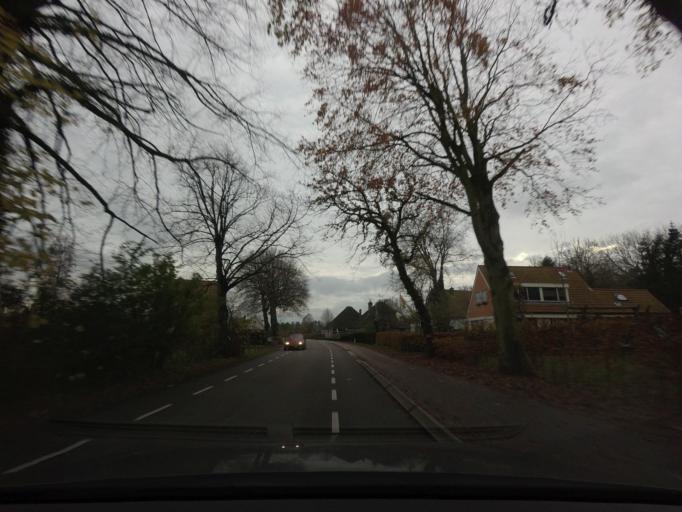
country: NL
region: North Holland
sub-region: Gemeente Bergen
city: Egmond aan Zee
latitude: 52.6371
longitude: 4.6569
